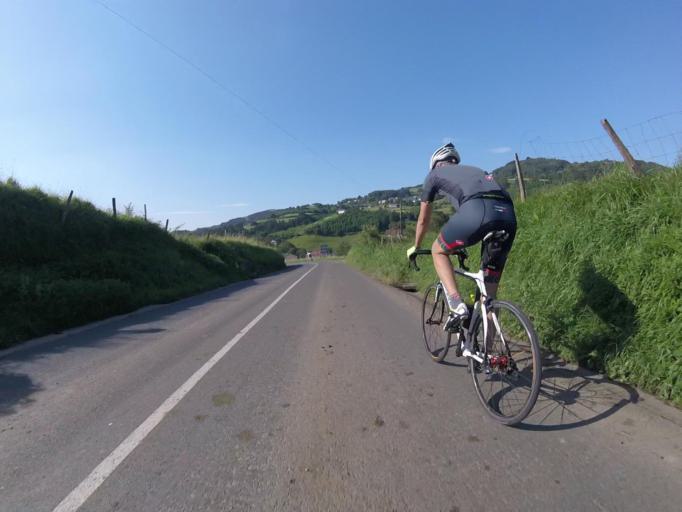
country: ES
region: Basque Country
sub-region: Provincia de Guipuzcoa
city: Asteasu
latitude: 43.1965
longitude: -2.0992
